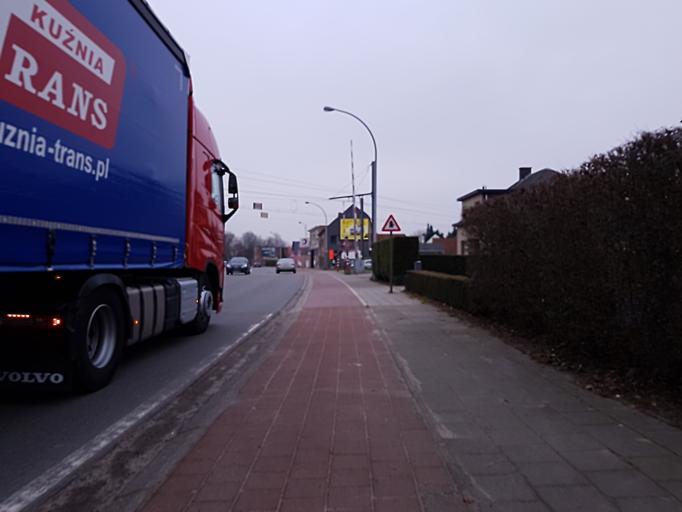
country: BE
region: Flanders
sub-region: Provincie Antwerpen
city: Willebroek
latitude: 51.0478
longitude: 4.3779
